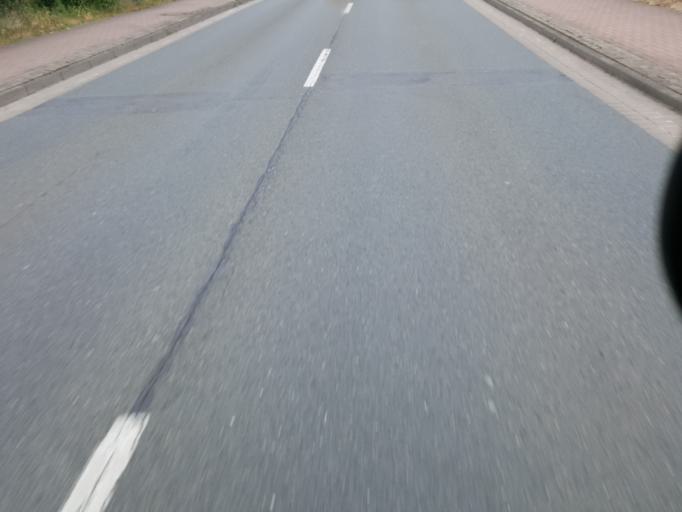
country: DE
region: Lower Saxony
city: Rehburg-Loccum
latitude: 52.4586
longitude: 9.1492
